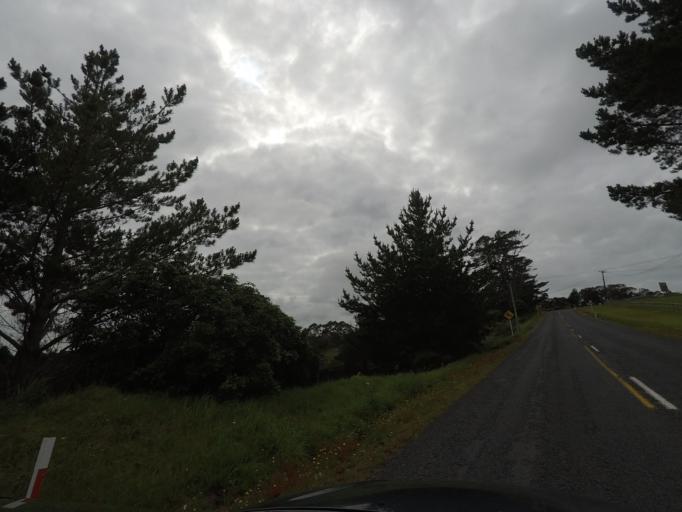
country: NZ
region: Auckland
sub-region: Auckland
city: Rosebank
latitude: -36.8369
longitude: 174.5814
